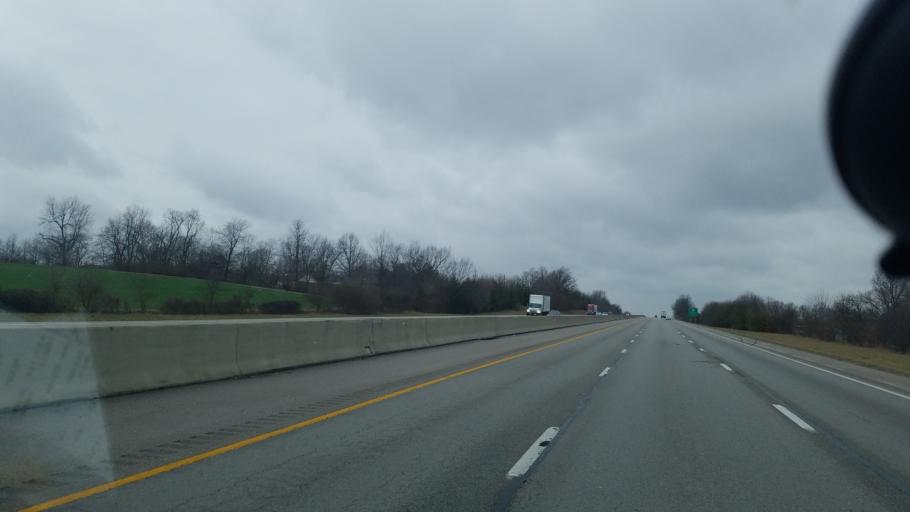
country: US
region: Kentucky
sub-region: Clark County
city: Winchester
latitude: 38.0357
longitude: -84.2788
